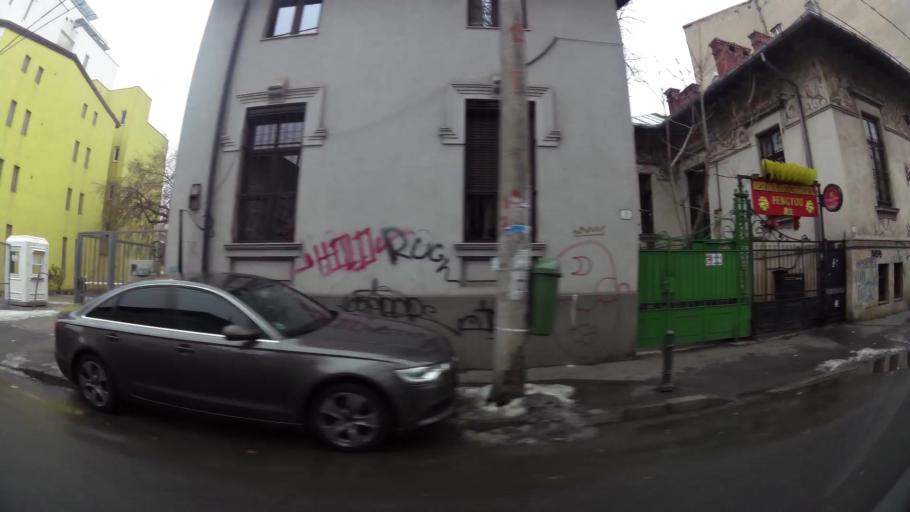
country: RO
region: Bucuresti
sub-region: Municipiul Bucuresti
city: Bucuresti
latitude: 44.4476
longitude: 26.0834
